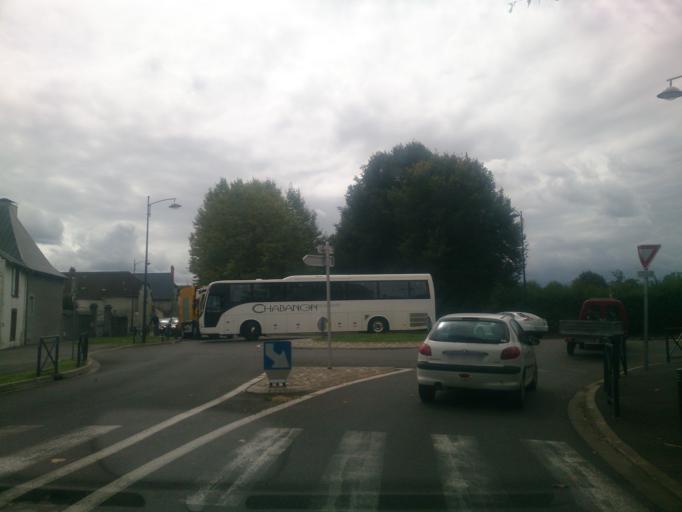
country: FR
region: Midi-Pyrenees
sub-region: Departement des Hautes-Pyrenees
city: Laloubere
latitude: 43.2050
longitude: 0.0740
